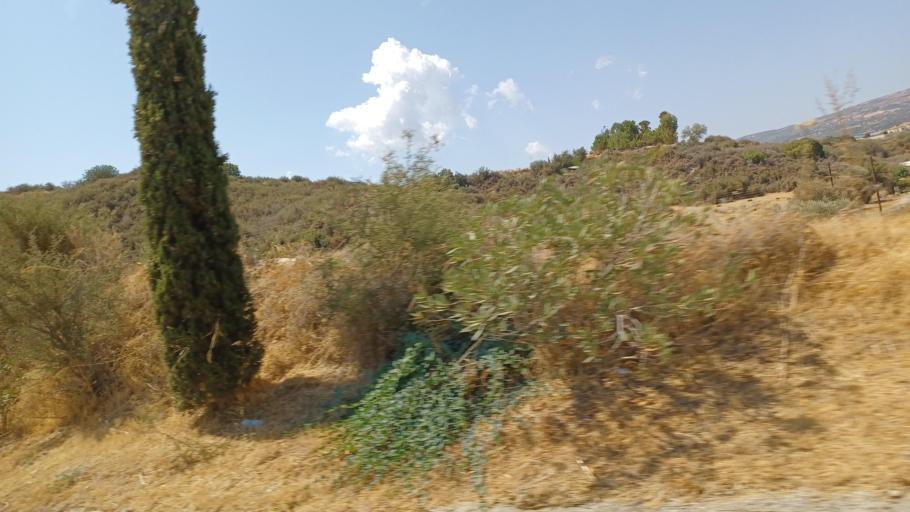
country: CY
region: Pafos
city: Polis
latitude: 35.0082
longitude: 32.4586
